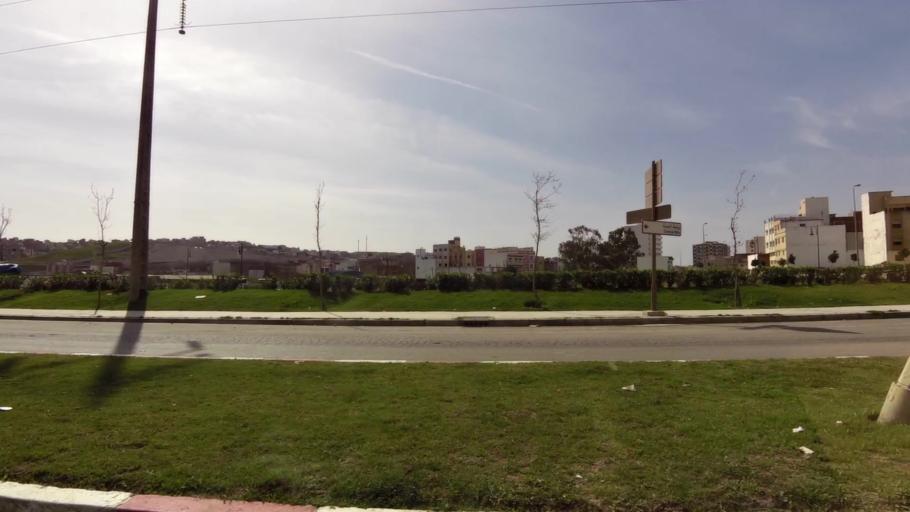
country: MA
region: Tanger-Tetouan
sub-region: Tanger-Assilah
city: Tangier
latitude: 35.7301
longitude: -5.8032
